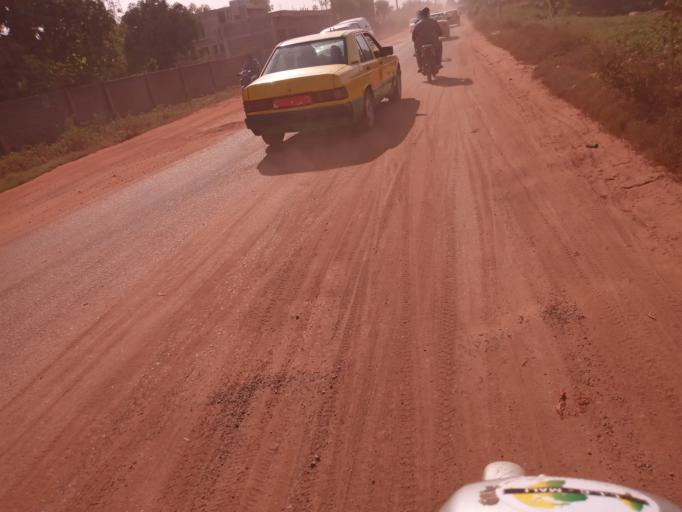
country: ML
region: Bamako
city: Bamako
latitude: 12.6355
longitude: -7.9305
